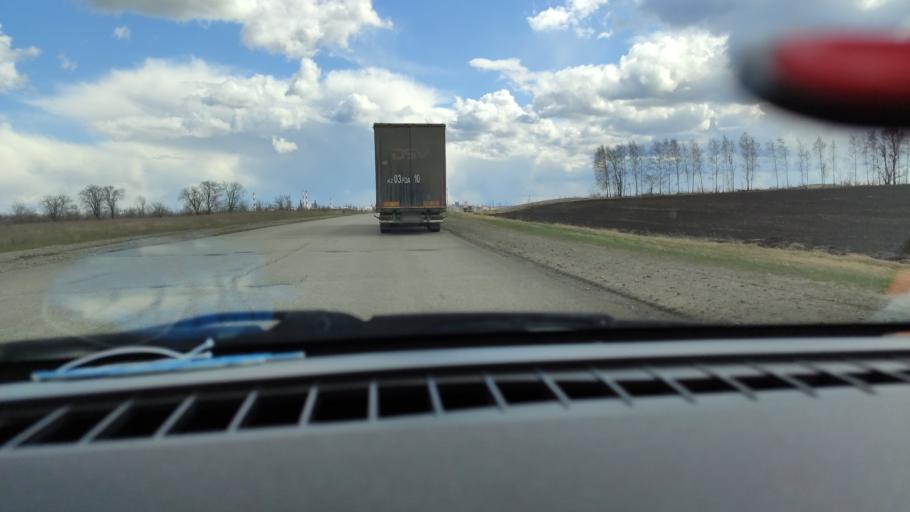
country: RU
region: Samara
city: Varlamovo
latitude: 53.1095
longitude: 48.3550
